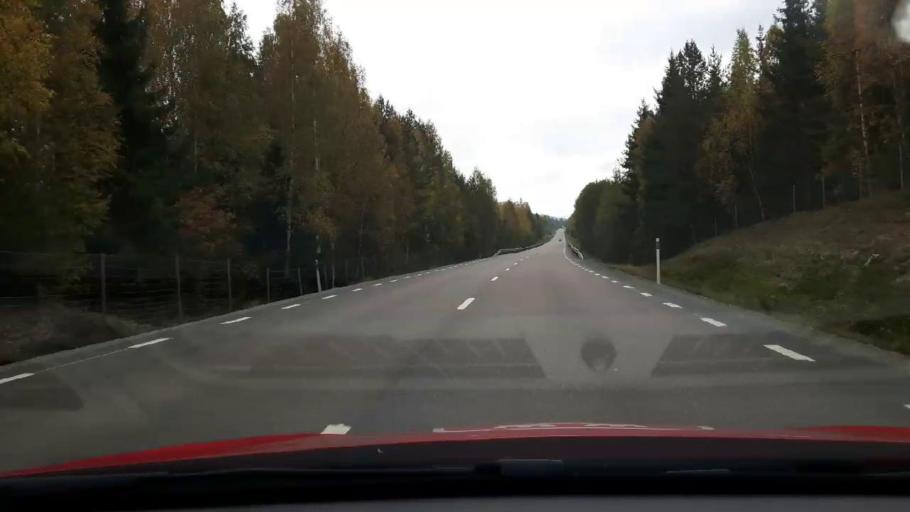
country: SE
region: Gaevleborg
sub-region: Bollnas Kommun
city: Kilafors
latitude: 61.2965
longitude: 16.4897
